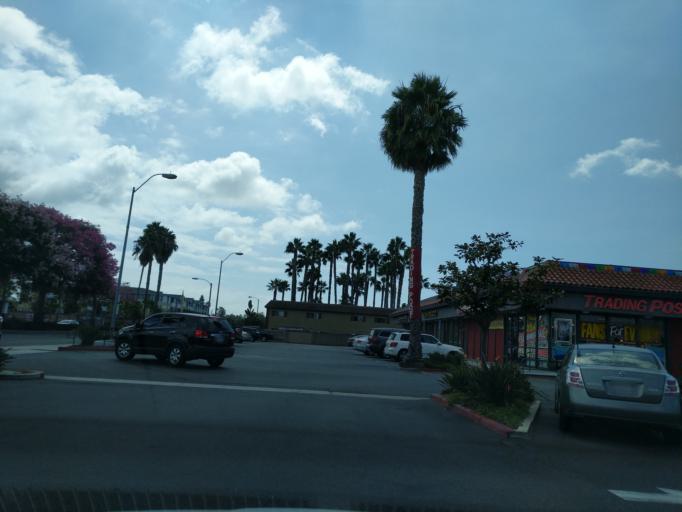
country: US
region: California
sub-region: Orange County
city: Midway City
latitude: 33.7148
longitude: -118.0069
